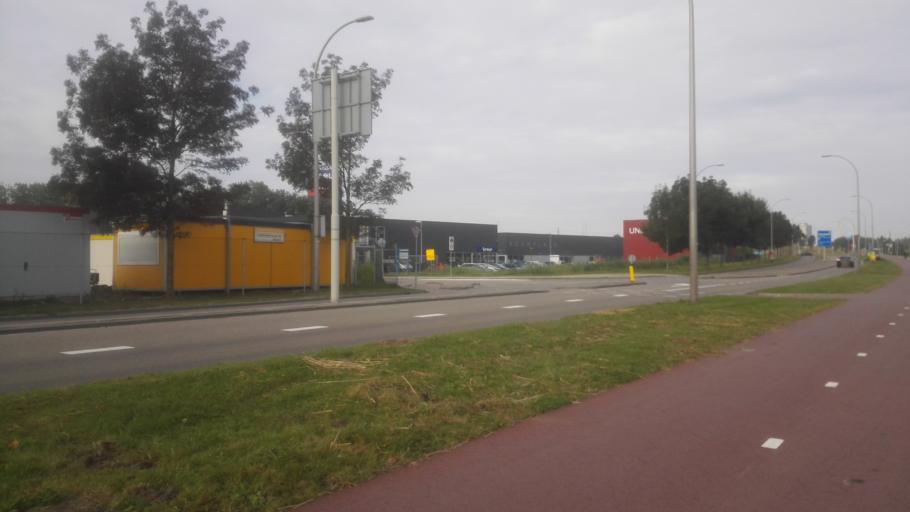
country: NL
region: South Holland
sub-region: Gemeente Den Haag
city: Ypenburg
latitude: 52.0303
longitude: 4.3604
